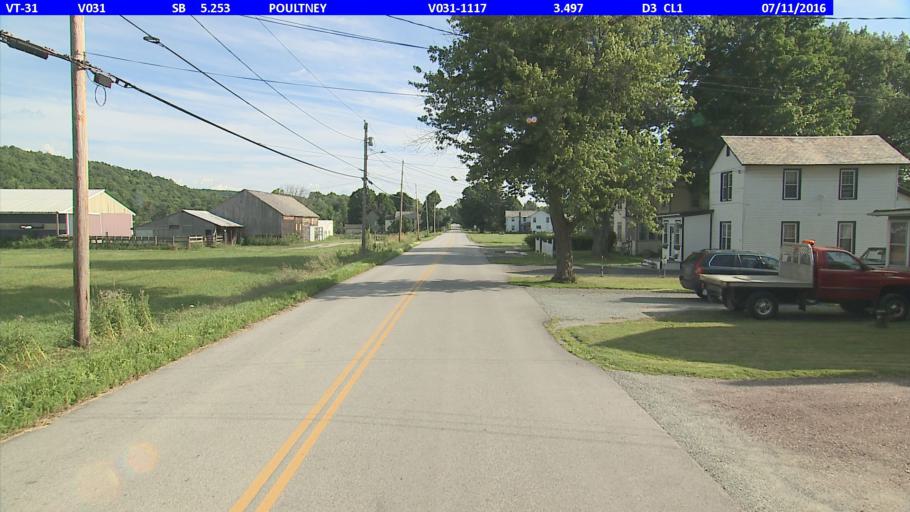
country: US
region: Vermont
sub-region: Rutland County
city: Poultney
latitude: 43.5118
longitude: -73.2337
